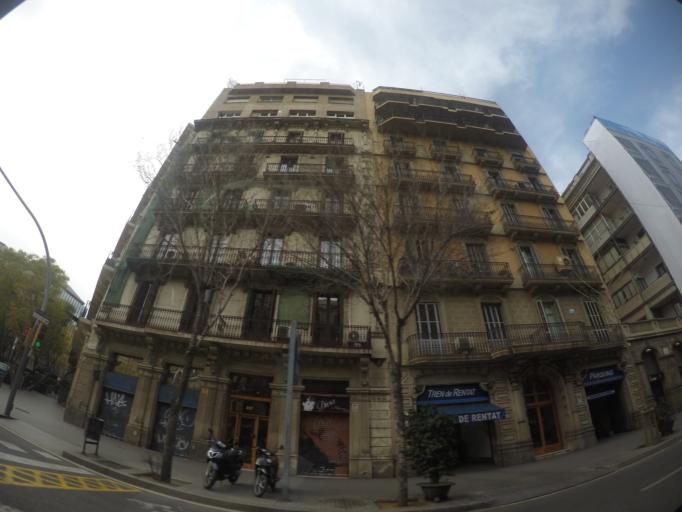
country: ES
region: Catalonia
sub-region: Provincia de Barcelona
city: Eixample
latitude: 41.3897
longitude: 2.1615
